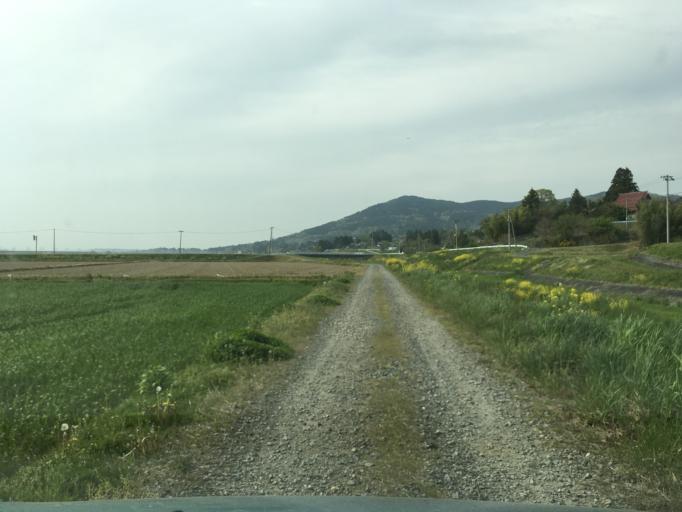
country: JP
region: Iwate
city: Ichinoseki
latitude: 38.9580
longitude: 141.1711
